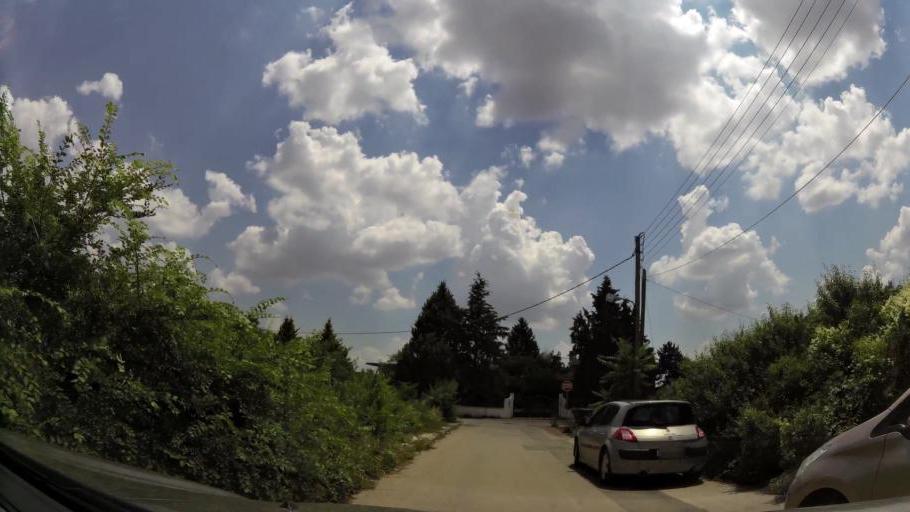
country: GR
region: West Macedonia
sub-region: Nomos Kozanis
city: Kozani
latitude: 40.2875
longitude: 21.7816
